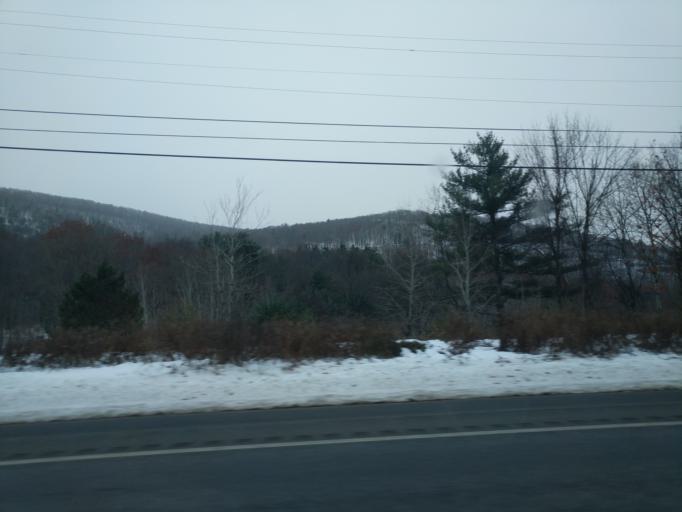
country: US
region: Pennsylvania
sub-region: Tioga County
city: Wellsboro
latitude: 41.8038
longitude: -77.2980
